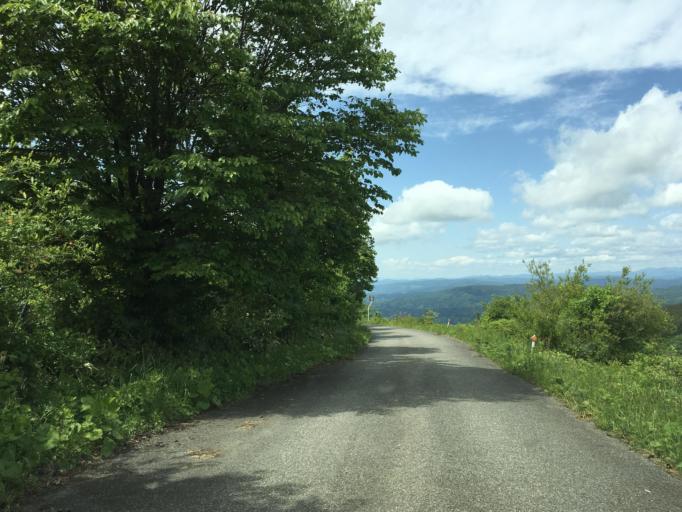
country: JP
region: Iwate
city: Mizusawa
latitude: 39.1323
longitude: 141.3168
